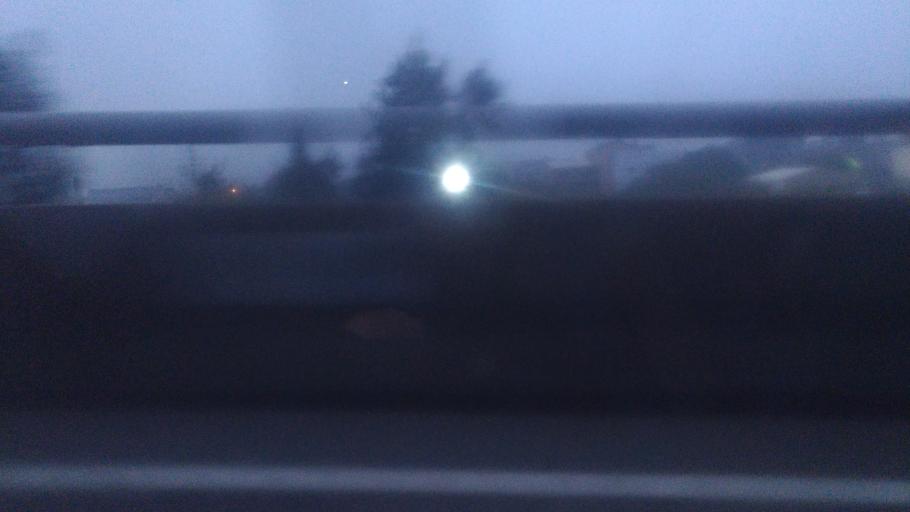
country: TW
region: Taiwan
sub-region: Miaoli
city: Miaoli
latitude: 24.4616
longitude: 120.6535
